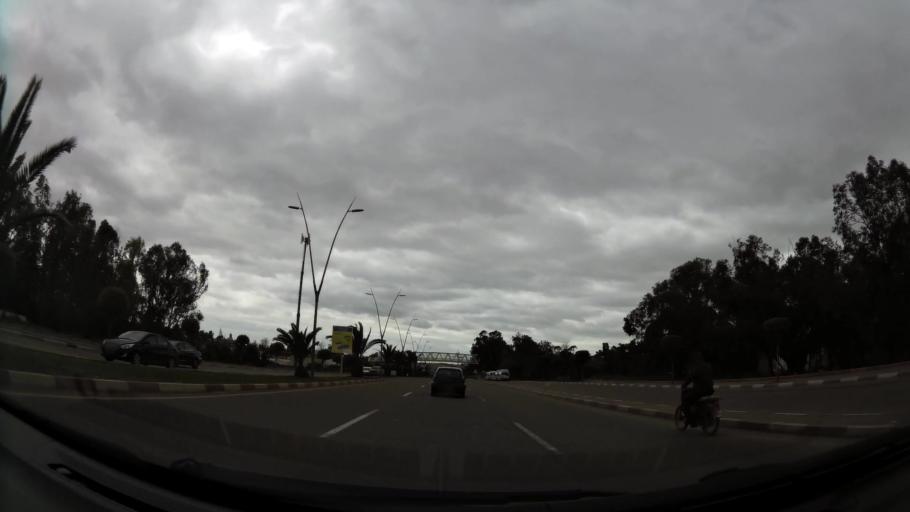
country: MA
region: Grand Casablanca
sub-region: Casablanca
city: Casablanca
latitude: 33.5285
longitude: -7.6367
